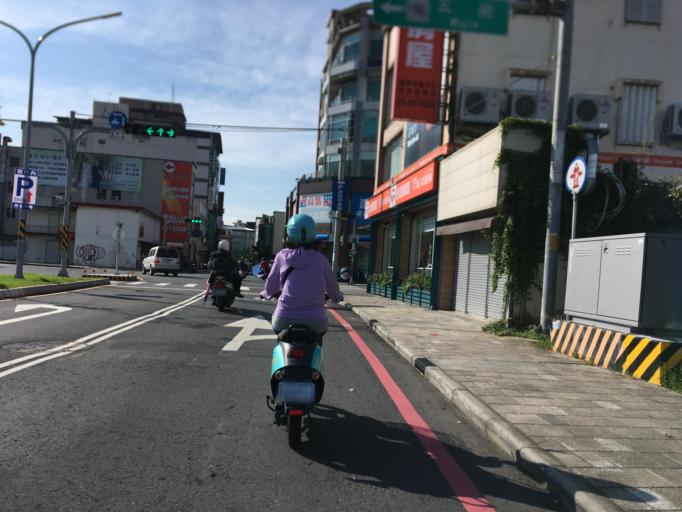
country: TW
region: Taiwan
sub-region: Yilan
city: Yilan
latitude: 24.6808
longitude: 121.7715
